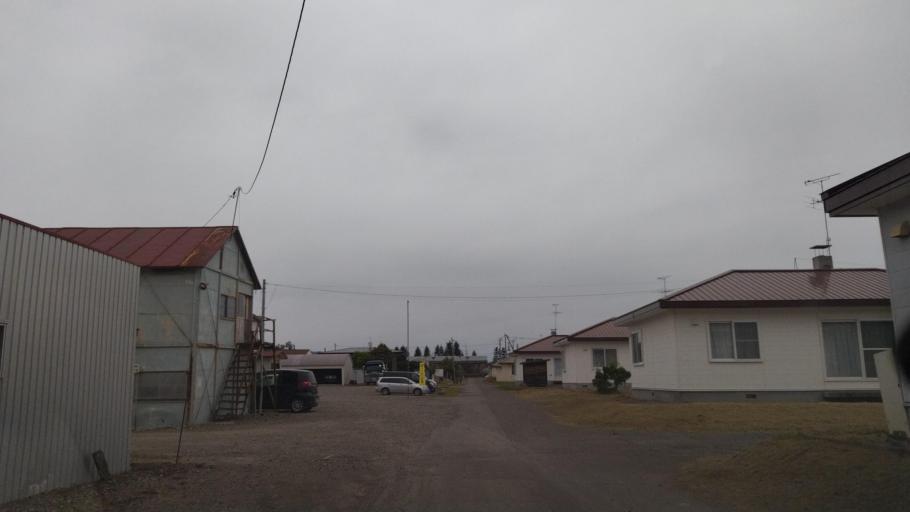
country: JP
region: Hokkaido
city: Otofuke
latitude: 43.2318
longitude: 143.2791
